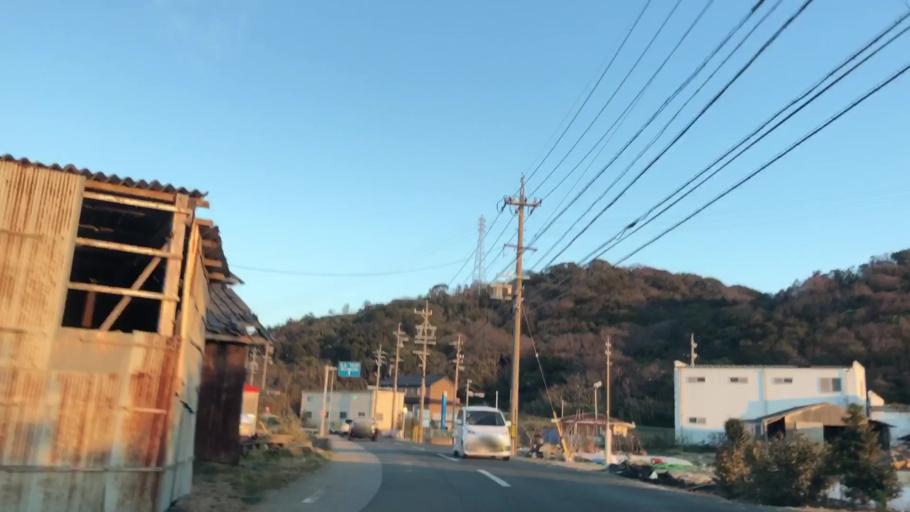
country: JP
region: Aichi
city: Toyohama
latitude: 34.6041
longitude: 137.0580
